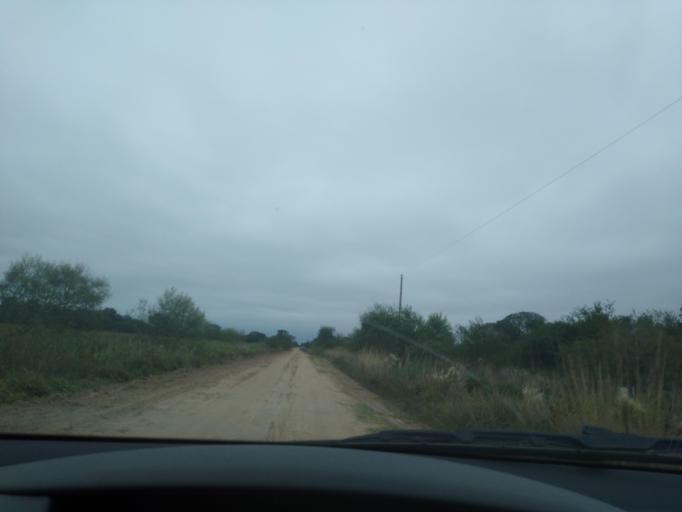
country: AR
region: Chaco
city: Colonia Benitez
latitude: -27.3676
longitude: -58.9513
